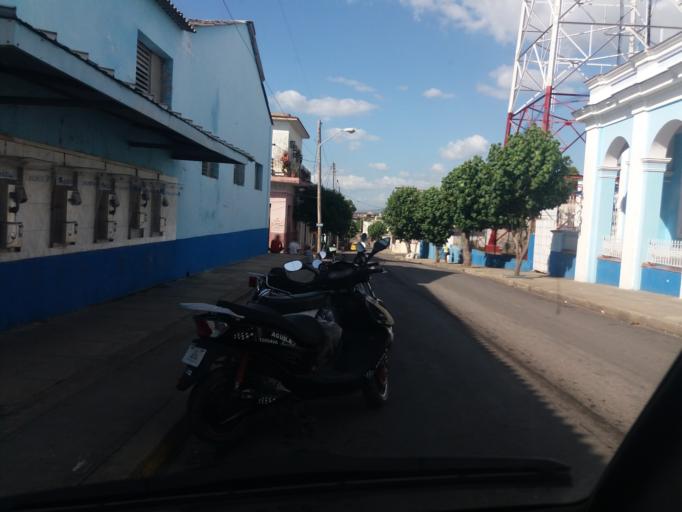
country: CU
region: Cienfuegos
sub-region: Municipio de Cienfuegos
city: Cienfuegos
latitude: 22.1467
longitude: -80.4453
